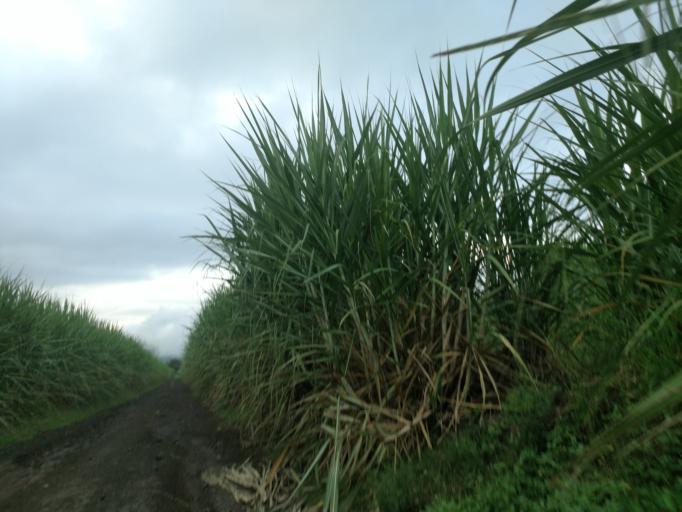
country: MX
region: Nayarit
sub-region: Tepic
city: La Corregidora
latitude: 21.4713
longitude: -104.8030
